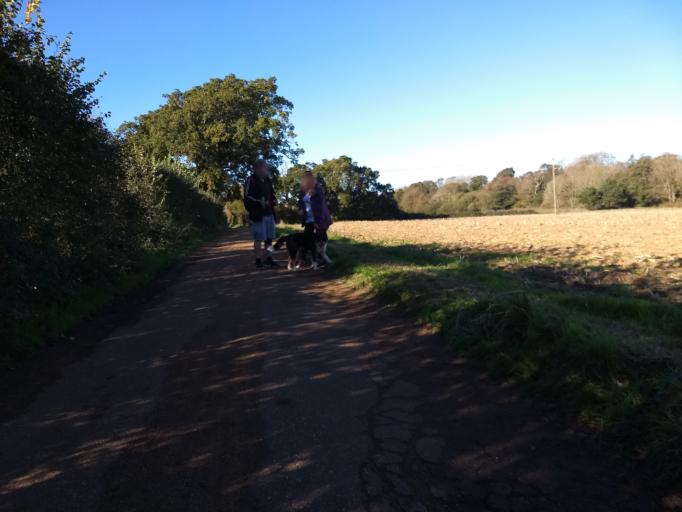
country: GB
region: England
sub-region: Isle of Wight
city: Newport
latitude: 50.6664
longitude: -1.2765
